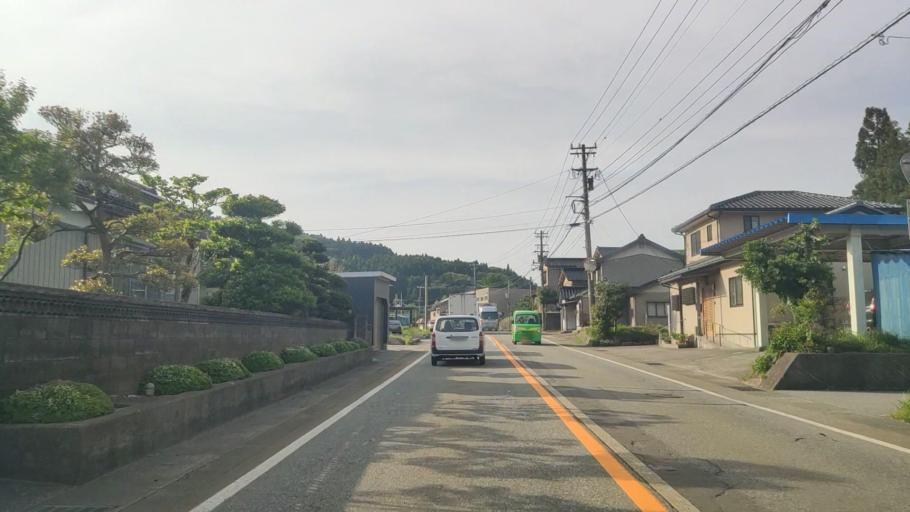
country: JP
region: Toyama
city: Yatsuomachi-higashikumisaka
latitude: 36.5378
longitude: 137.2306
